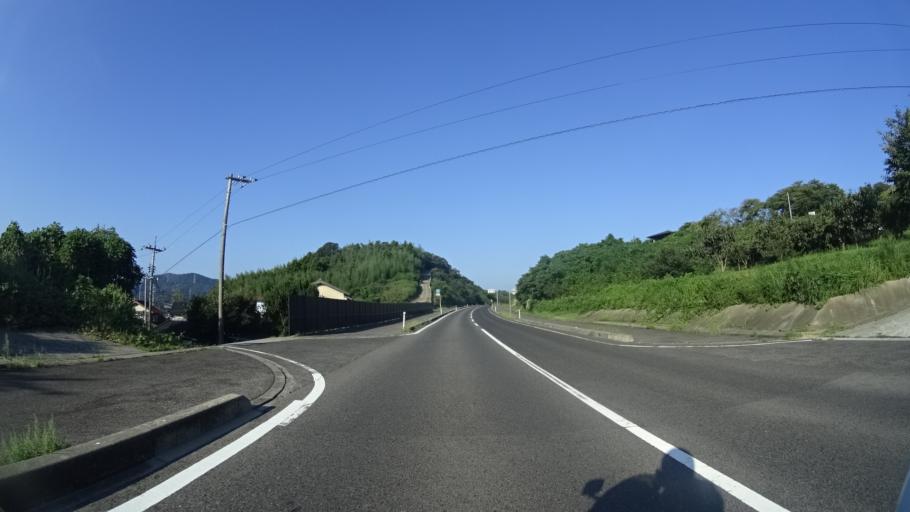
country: JP
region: Shimane
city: Matsue-shi
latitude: 35.5164
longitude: 133.1338
